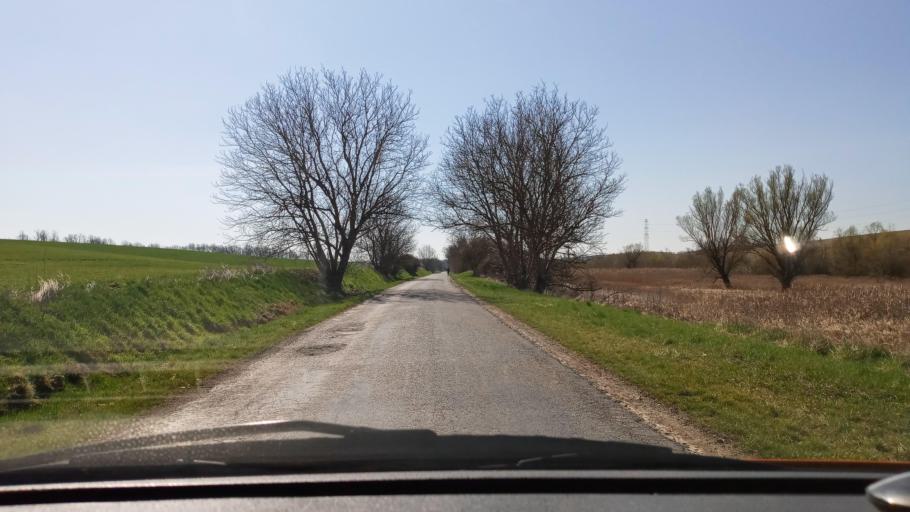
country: HU
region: Baranya
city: Kozarmisleny
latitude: 46.0537
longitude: 18.3782
